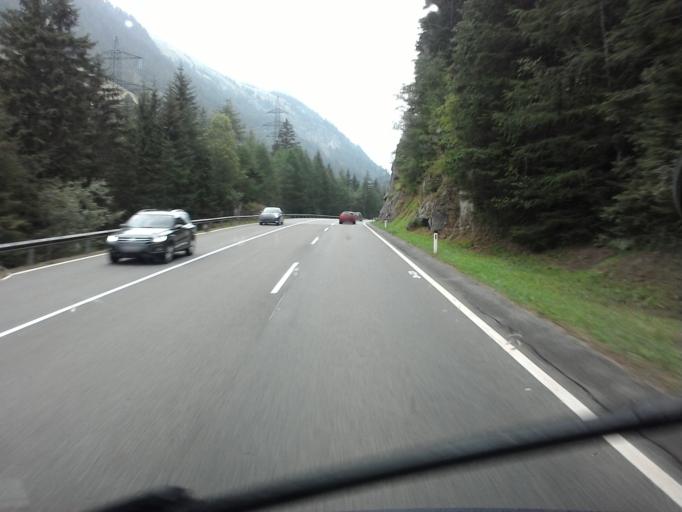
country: AT
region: Tyrol
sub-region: Politischer Bezirk Lienz
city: Matrei in Osttirol
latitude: 47.0469
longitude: 12.5160
